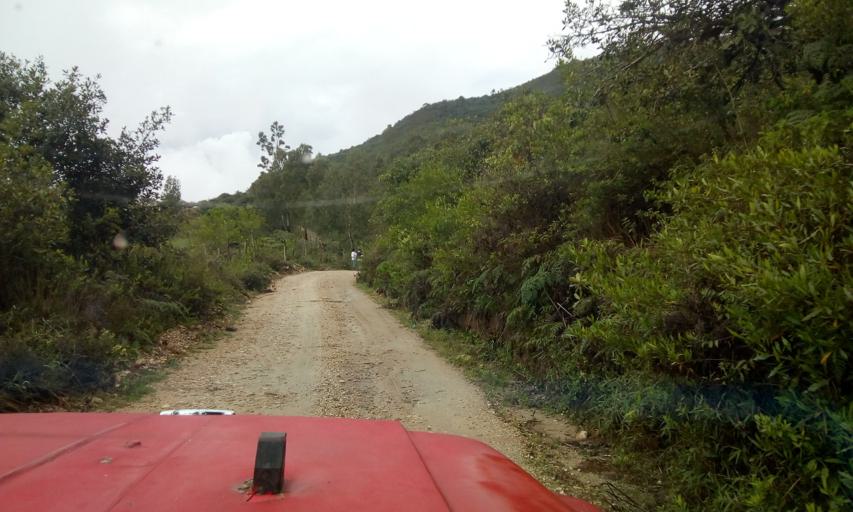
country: CO
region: Boyaca
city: Tipacoque
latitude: 6.4232
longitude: -72.6917
